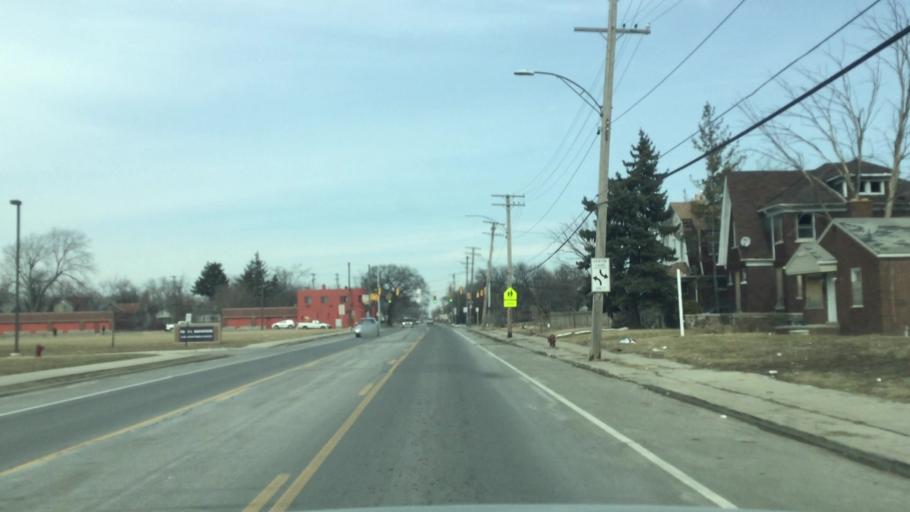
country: US
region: Michigan
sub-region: Wayne County
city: Dearborn
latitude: 42.3648
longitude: -83.1581
